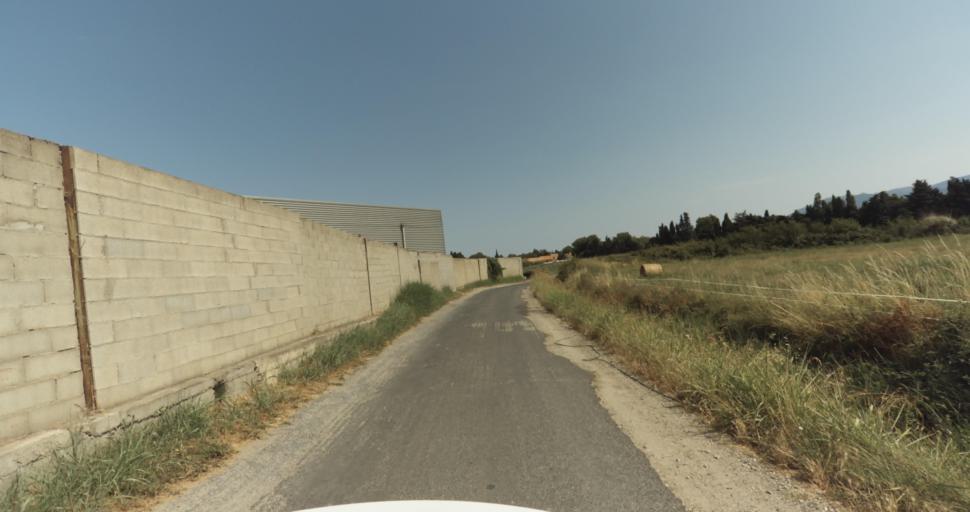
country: FR
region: Languedoc-Roussillon
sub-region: Departement des Pyrenees-Orientales
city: Latour-Bas-Elne
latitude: 42.6059
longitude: 2.9946
